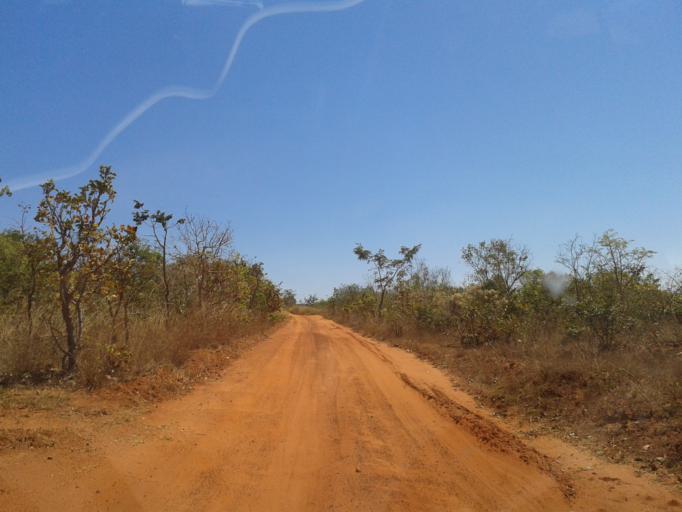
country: BR
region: Minas Gerais
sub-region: Ituiutaba
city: Ituiutaba
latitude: -19.1111
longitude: -49.2818
